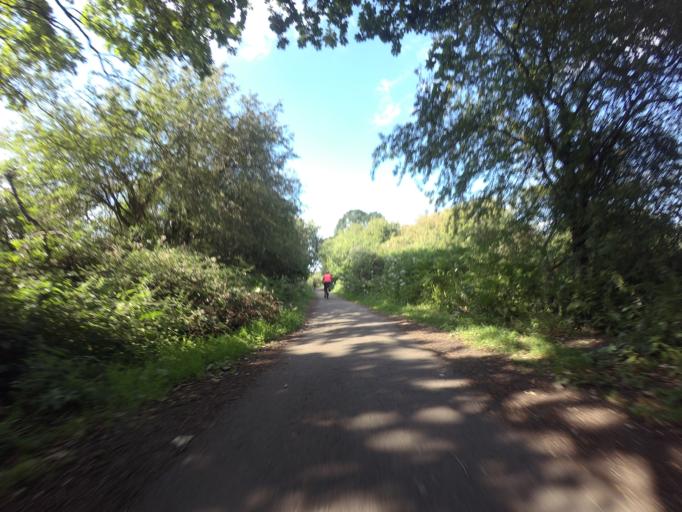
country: GB
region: England
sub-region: East Sussex
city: Hailsham
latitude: 50.8830
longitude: 0.2505
